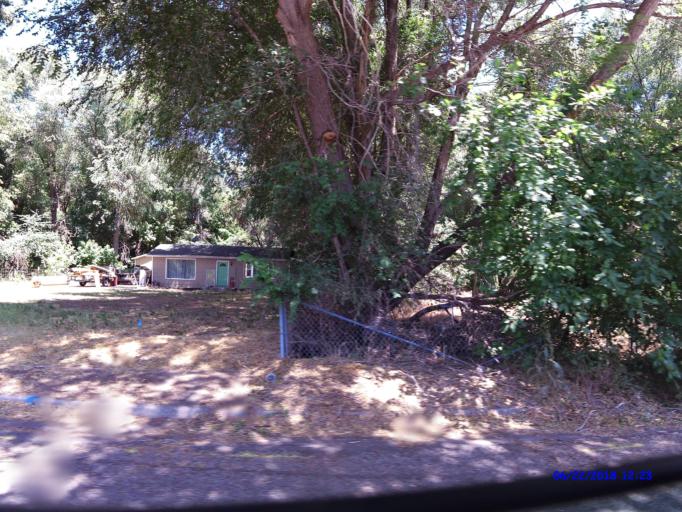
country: US
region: Utah
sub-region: Weber County
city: Ogden
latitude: 41.2413
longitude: -111.9681
